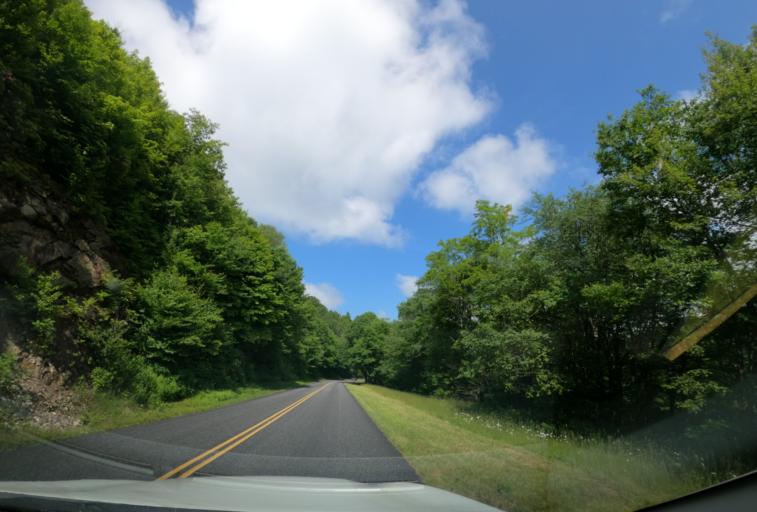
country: US
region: North Carolina
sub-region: Haywood County
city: Hazelwood
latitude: 35.3959
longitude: -83.0402
